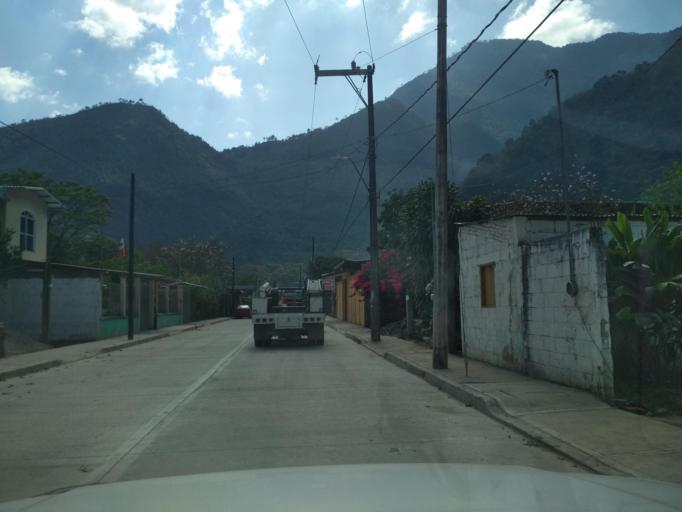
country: MX
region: Veracruz
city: Jalapilla
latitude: 18.8040
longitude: -97.1024
